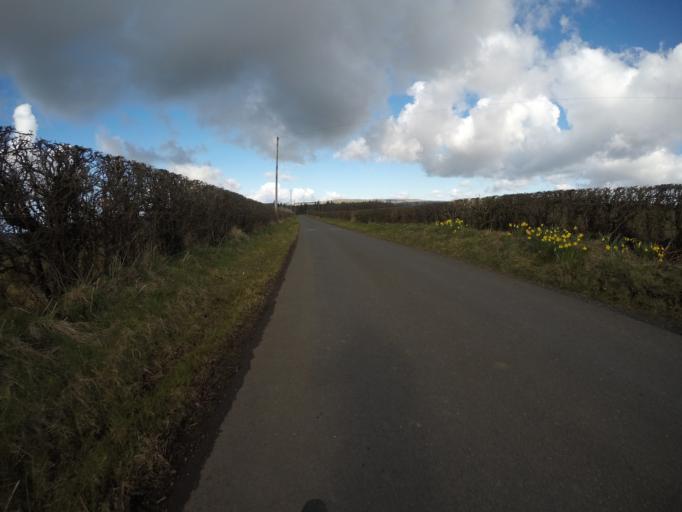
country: GB
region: Scotland
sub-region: North Ayrshire
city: Kilwinning
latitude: 55.6895
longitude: -4.6680
